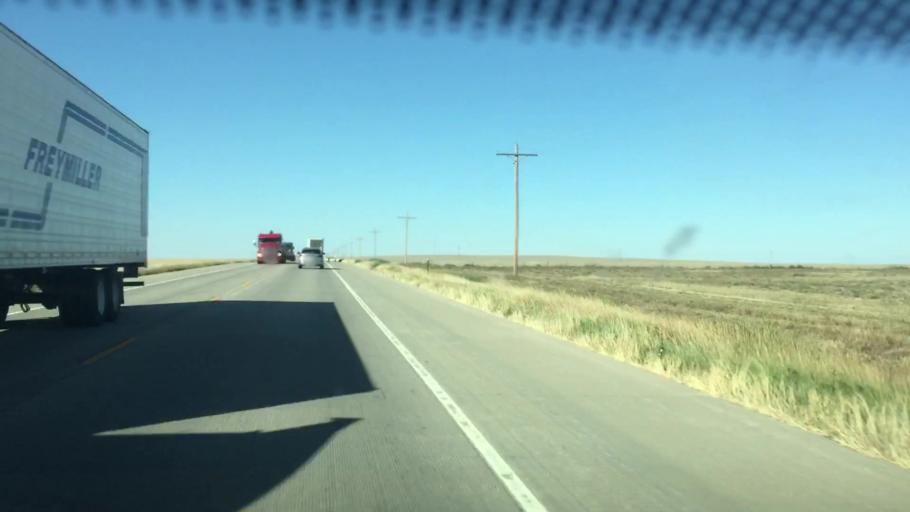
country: US
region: Colorado
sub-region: Prowers County
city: Lamar
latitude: 38.2514
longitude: -102.7240
